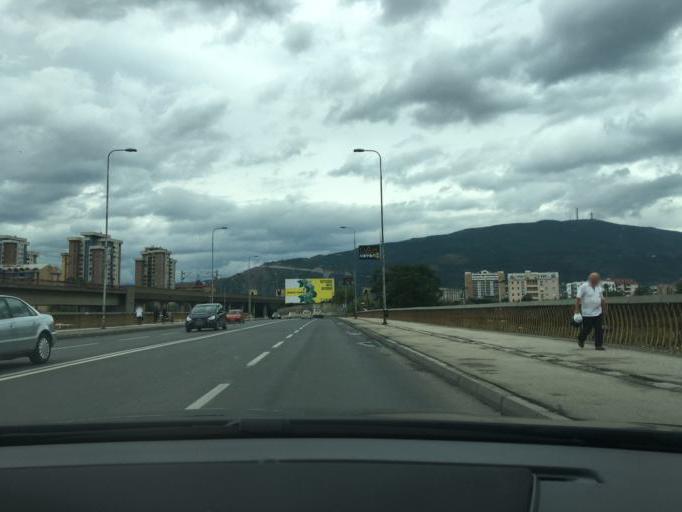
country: MK
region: Karpos
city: Skopje
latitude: 41.9955
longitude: 21.4496
